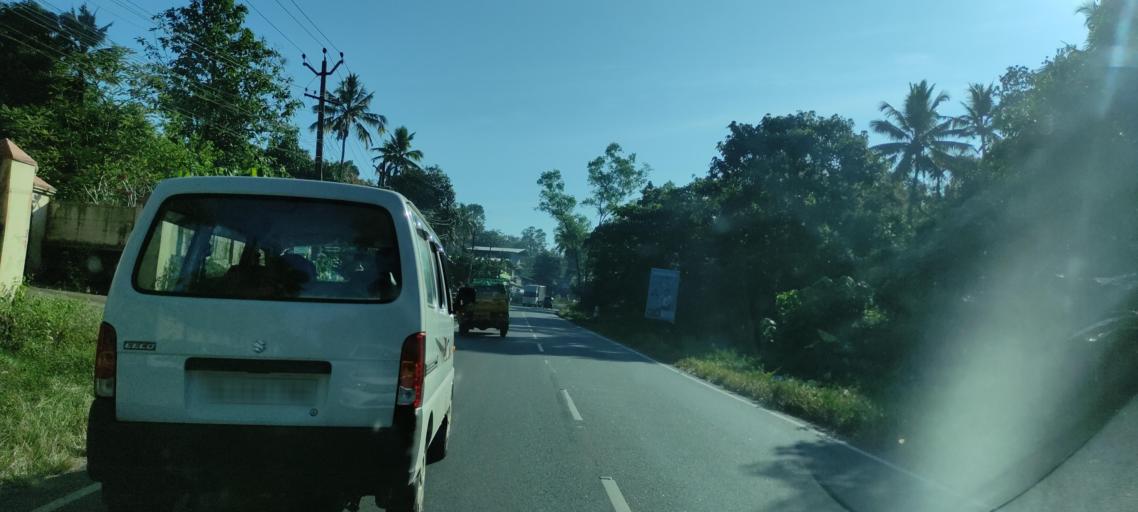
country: IN
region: Kerala
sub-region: Alappuzha
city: Kattanam
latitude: 9.1750
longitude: 76.6252
